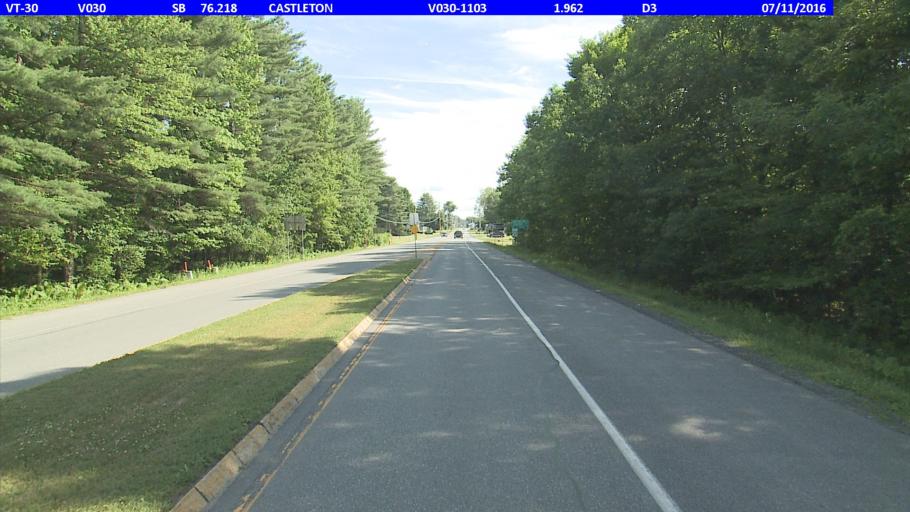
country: US
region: Vermont
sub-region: Rutland County
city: Castleton
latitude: 43.6149
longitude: -73.2071
